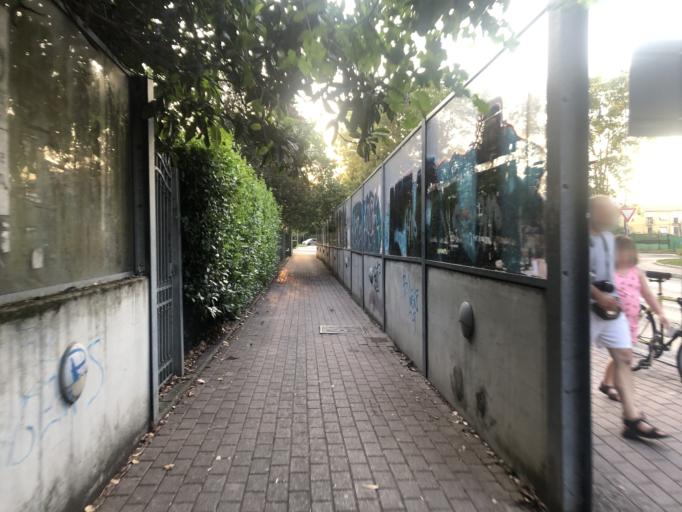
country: IT
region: Tuscany
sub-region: Province of Pisa
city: Pisa
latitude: 43.7244
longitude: 10.4101
